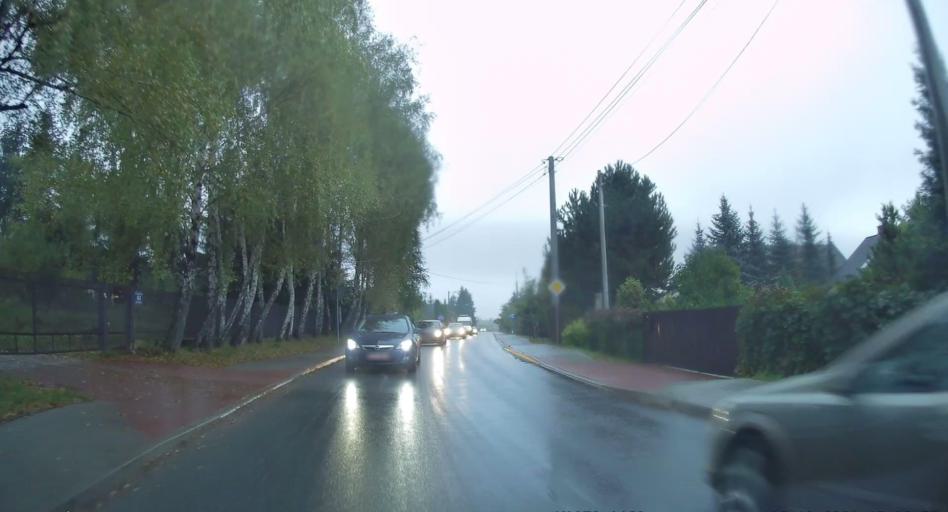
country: PL
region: Lesser Poland Voivodeship
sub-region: Powiat krakowski
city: Ochojno
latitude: 49.9562
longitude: 19.9789
